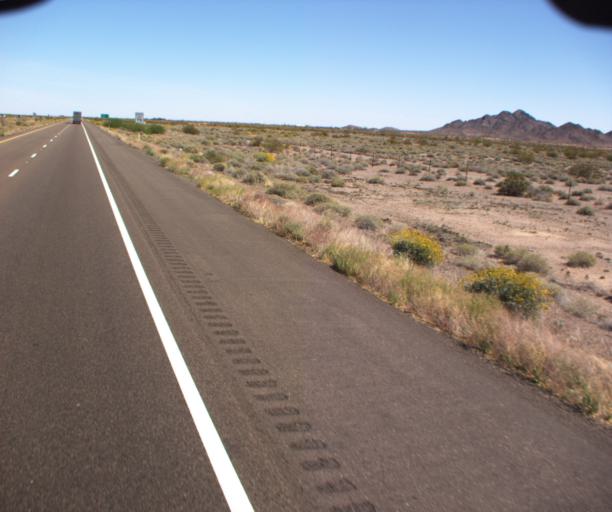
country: US
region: Arizona
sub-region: Yuma County
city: Wellton
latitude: 32.8050
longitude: -113.5289
